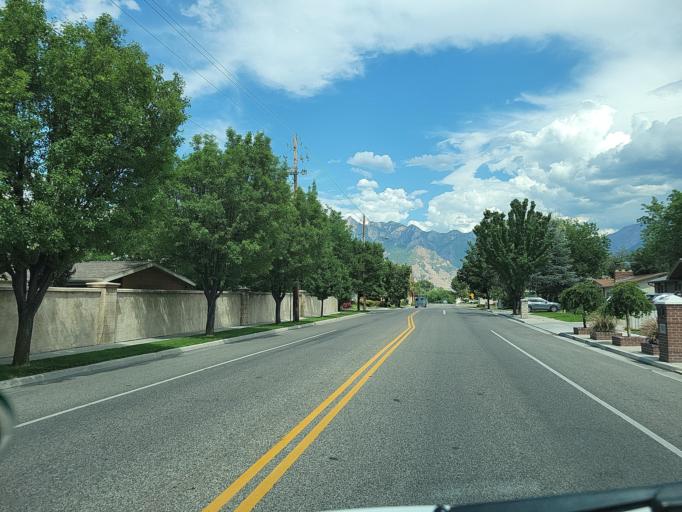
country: US
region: Utah
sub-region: Salt Lake County
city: Murray
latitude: 40.6417
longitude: -111.8712
